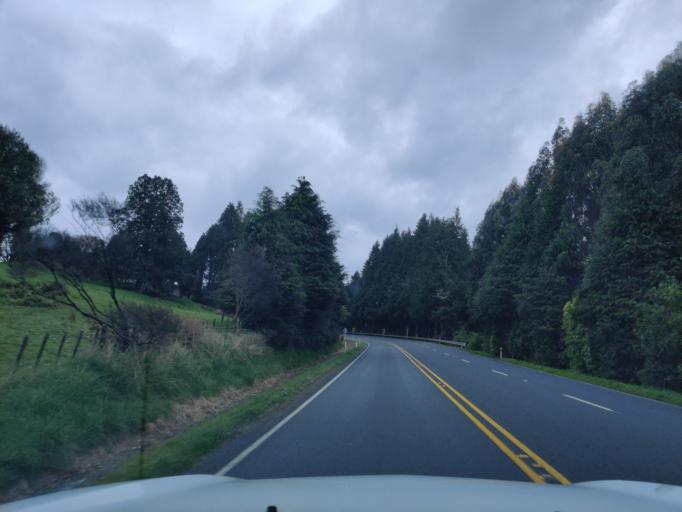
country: NZ
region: Waikato
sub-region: Otorohanga District
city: Otorohanga
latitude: -38.5002
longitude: 175.2014
